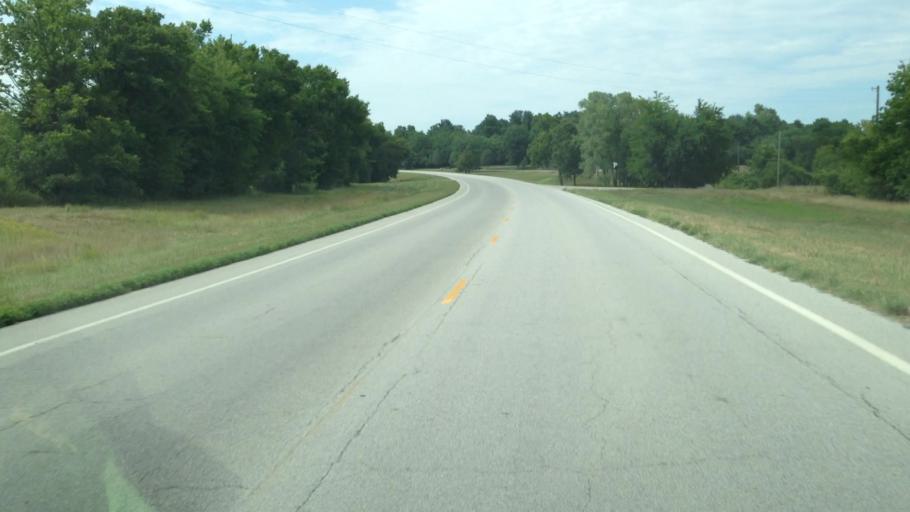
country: US
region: Kansas
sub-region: Labette County
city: Oswego
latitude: 37.1458
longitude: -95.1037
